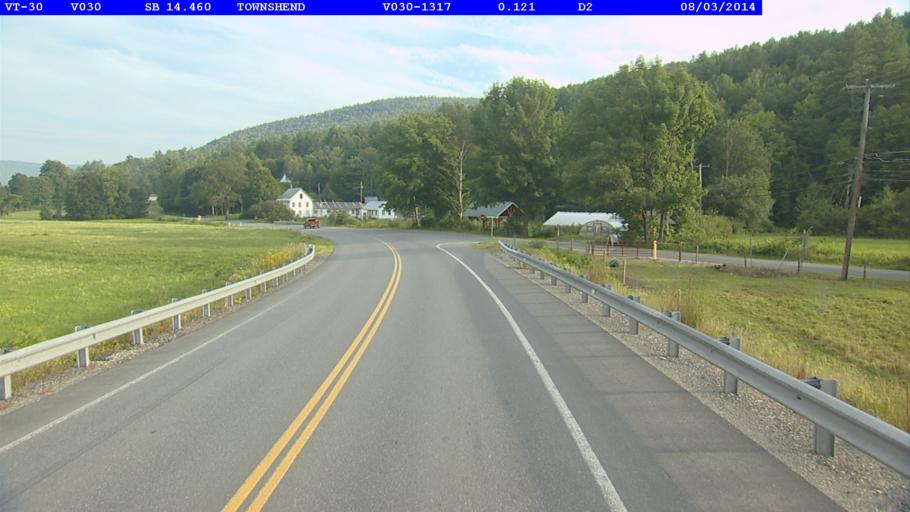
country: US
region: Vermont
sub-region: Windham County
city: Newfane
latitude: 43.0210
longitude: -72.6574
